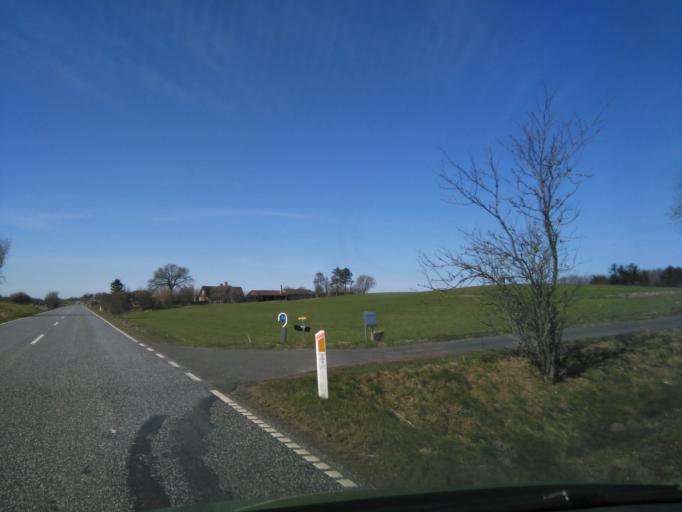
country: DK
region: Central Jutland
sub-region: Horsens Kommune
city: Braedstrup
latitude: 56.0222
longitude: 9.5948
